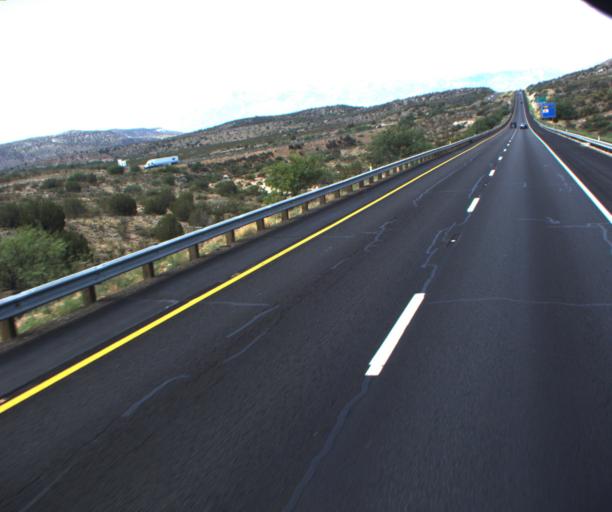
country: US
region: Arizona
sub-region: Yavapai County
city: Lake Montezuma
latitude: 34.6286
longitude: -111.8374
